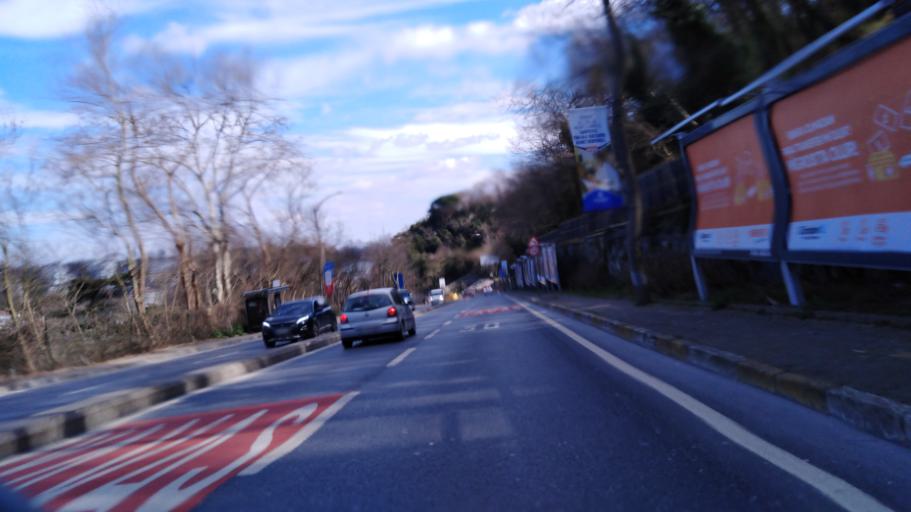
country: TR
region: Istanbul
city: Sisli
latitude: 41.1114
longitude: 29.0540
